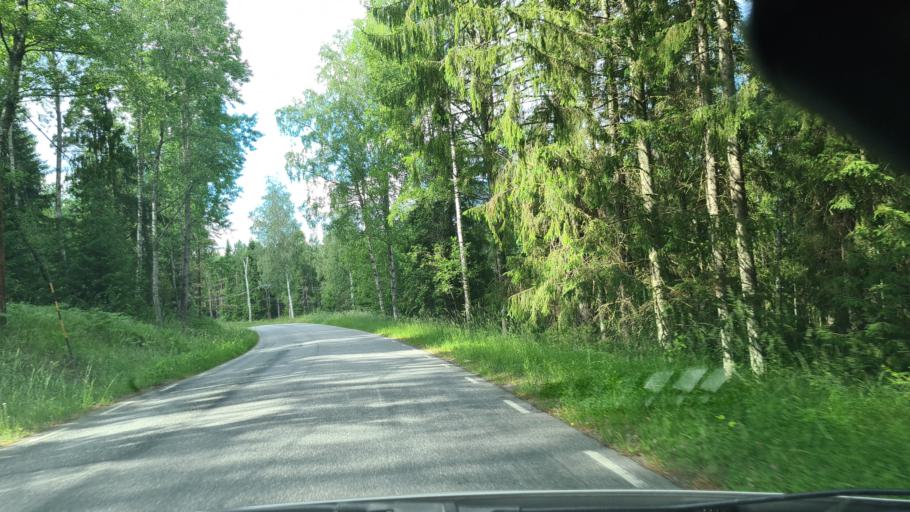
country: SE
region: Stockholm
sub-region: Varmdo Kommun
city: Mortnas
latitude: 59.4010
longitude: 18.4628
